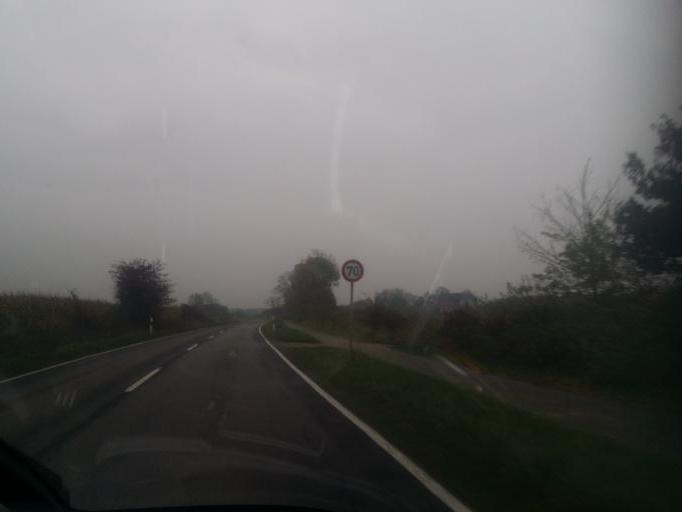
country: DE
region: Schleswig-Holstein
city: Grosssolt
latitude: 54.6957
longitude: 9.5102
